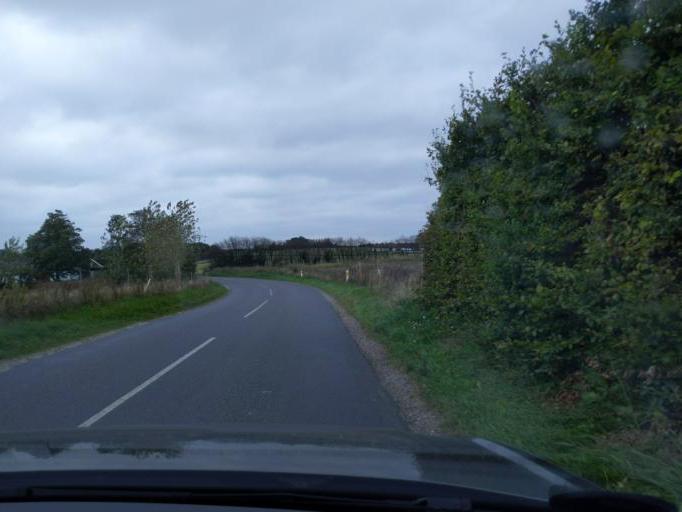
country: DK
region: Central Jutland
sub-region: Viborg Kommune
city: Bjerringbro
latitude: 56.5380
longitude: 9.6021
